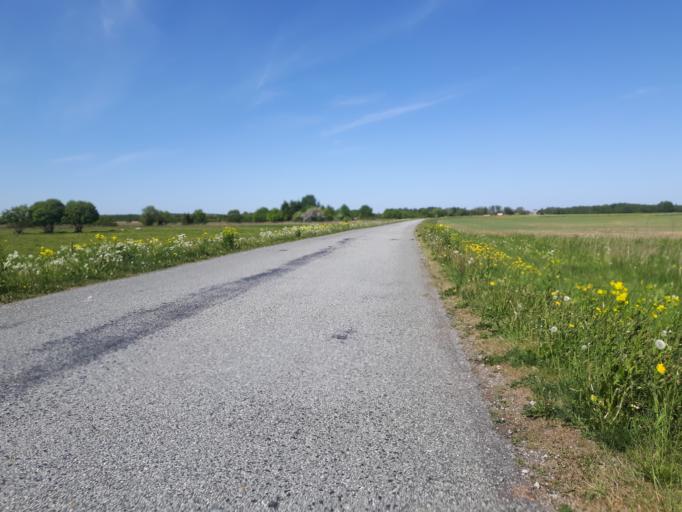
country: EE
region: Ida-Virumaa
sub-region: Aseri vald
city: Aseri
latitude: 59.4712
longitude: 26.8103
